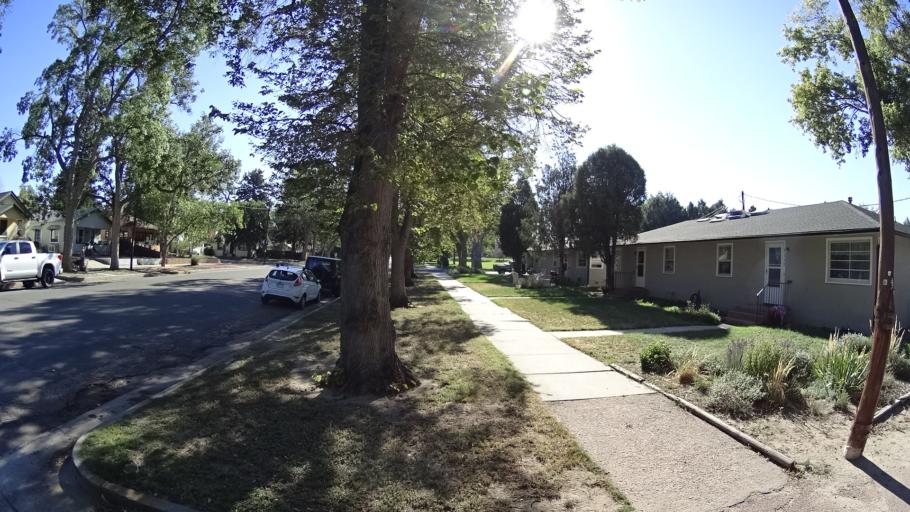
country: US
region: Colorado
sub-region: El Paso County
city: Colorado Springs
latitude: 38.8402
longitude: -104.8042
